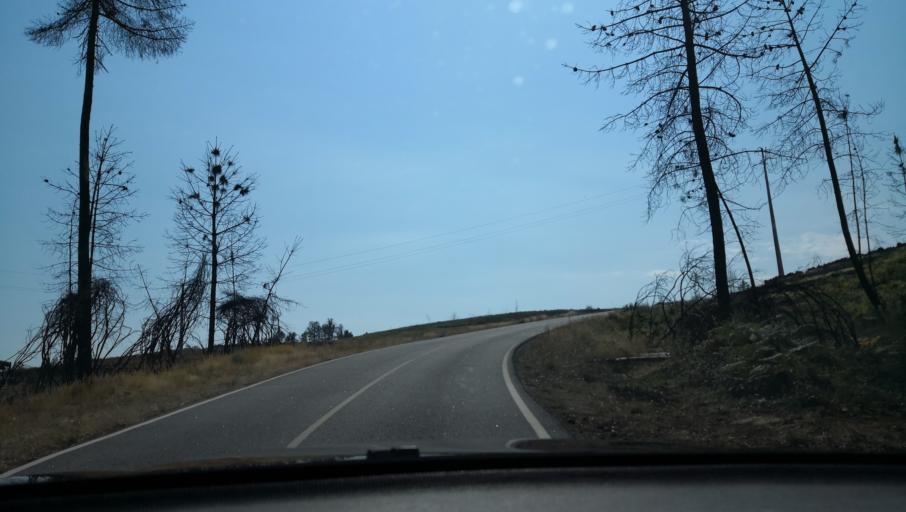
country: PT
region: Vila Real
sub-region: Sabrosa
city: Sabrosa
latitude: 41.3405
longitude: -7.5944
